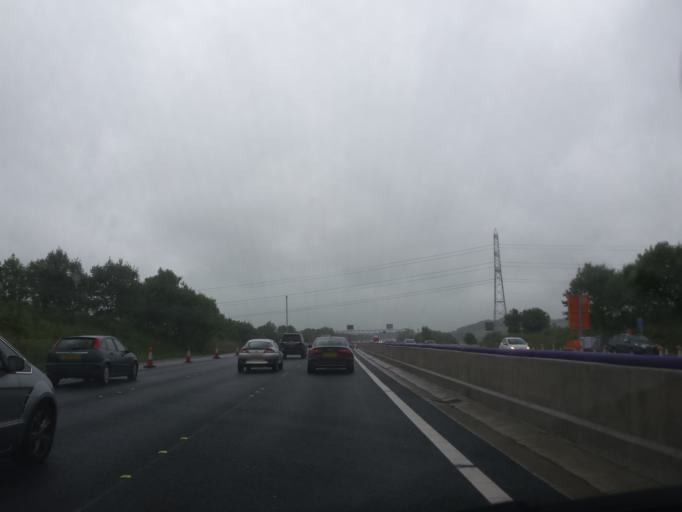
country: GB
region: England
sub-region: Derbyshire
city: Bolsover
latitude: 53.2118
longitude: -1.3232
